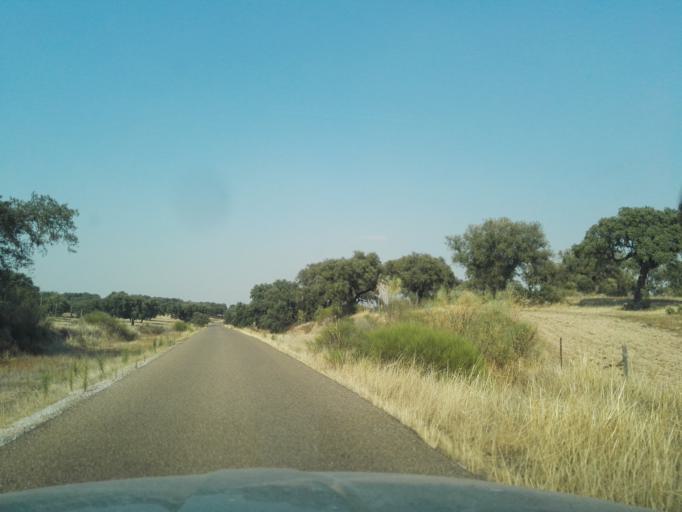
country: PT
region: Portalegre
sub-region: Campo Maior
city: Campo Maior
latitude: 38.9919
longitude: -7.1668
